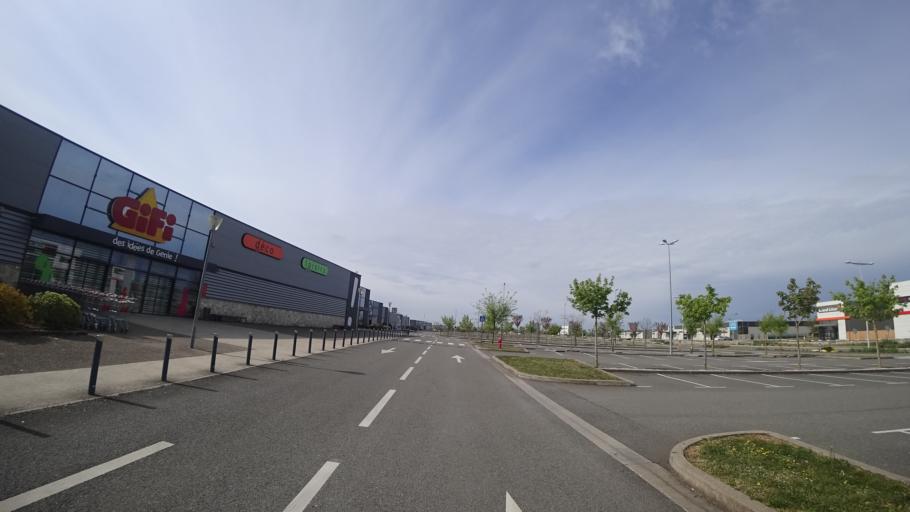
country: FR
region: Midi-Pyrenees
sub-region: Departement de l'Aveyron
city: Sebazac-Concoures
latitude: 44.3970
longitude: 2.6065
